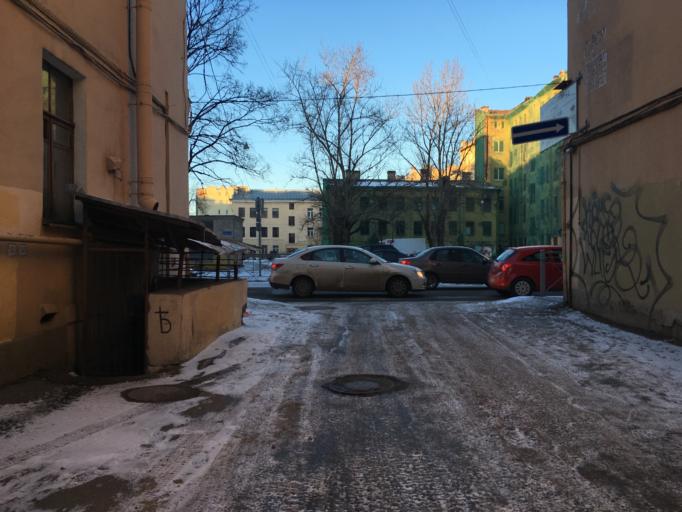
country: RU
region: St.-Petersburg
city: Centralniy
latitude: 59.9077
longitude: 30.3444
